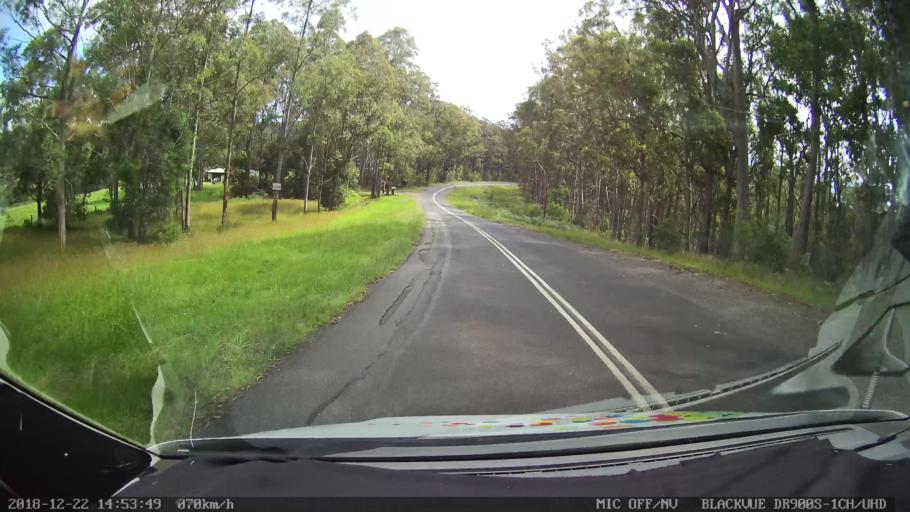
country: AU
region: New South Wales
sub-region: Bellingen
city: Dorrigo
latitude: -30.2216
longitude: 152.5380
